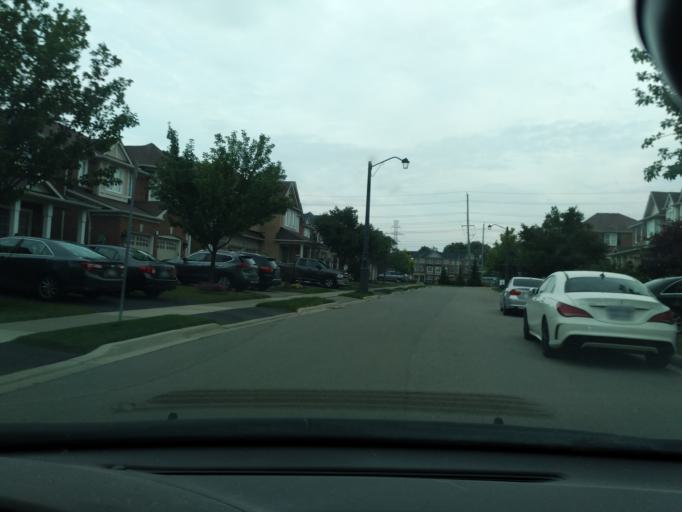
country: CA
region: Ontario
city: Newmarket
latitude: 44.0521
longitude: -79.4984
